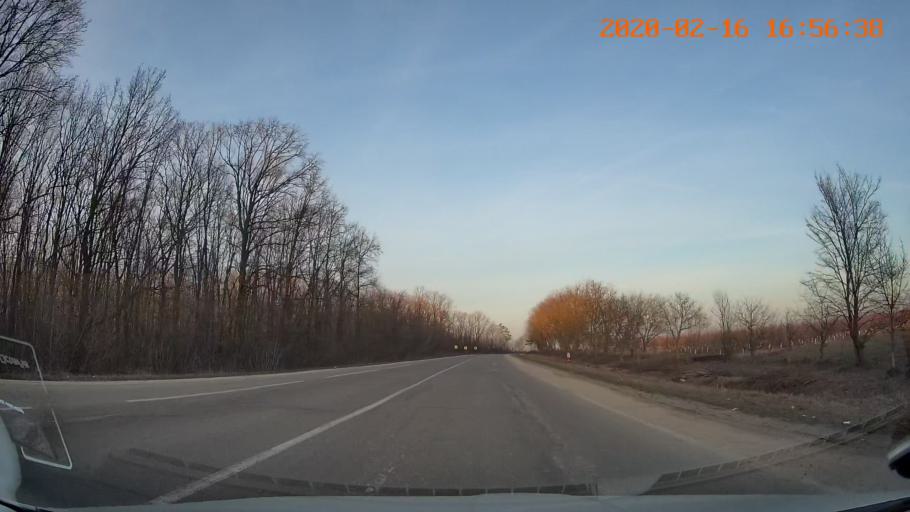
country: MD
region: Briceni
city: Briceni
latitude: 48.3354
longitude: 27.0531
